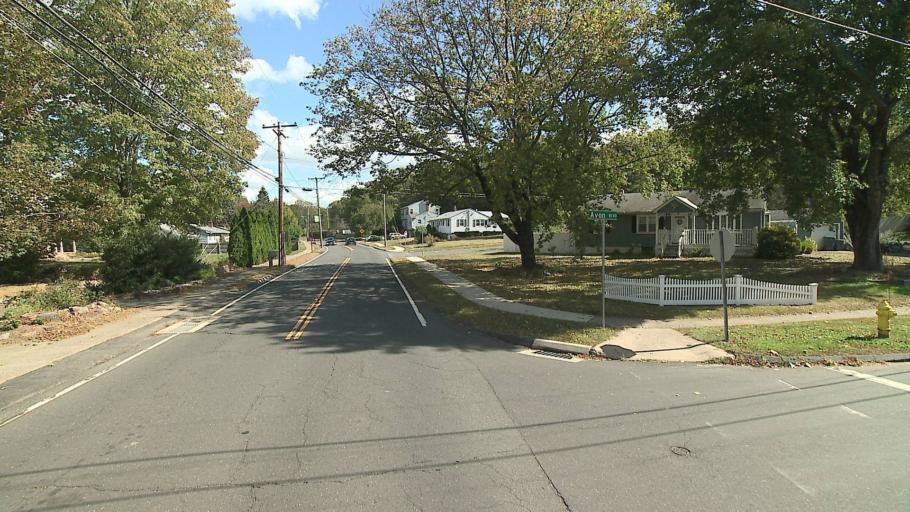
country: US
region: Connecticut
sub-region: New Haven County
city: Cheshire
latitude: 41.4777
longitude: -72.9167
